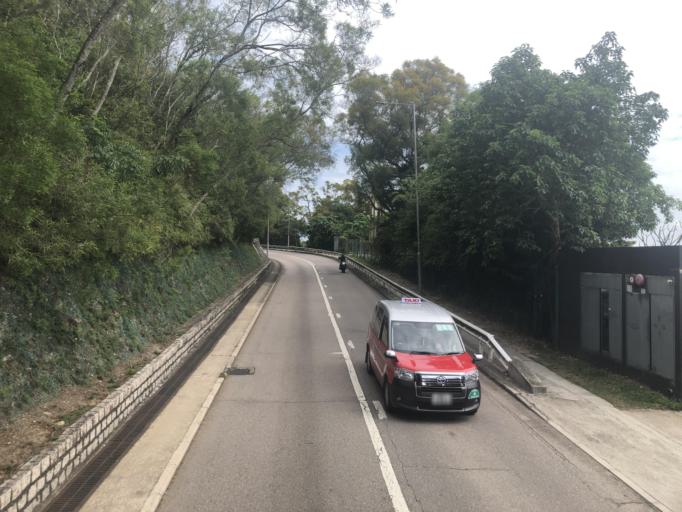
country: HK
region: Sai Kung
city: Sai Kung
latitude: 22.3876
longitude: 114.3032
